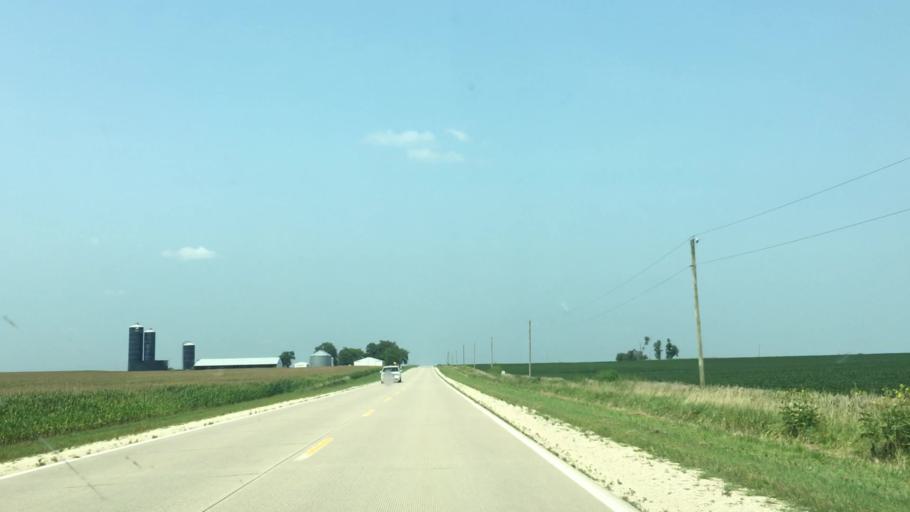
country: US
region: Iowa
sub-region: Fayette County
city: Fayette
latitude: 42.7393
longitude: -91.8040
